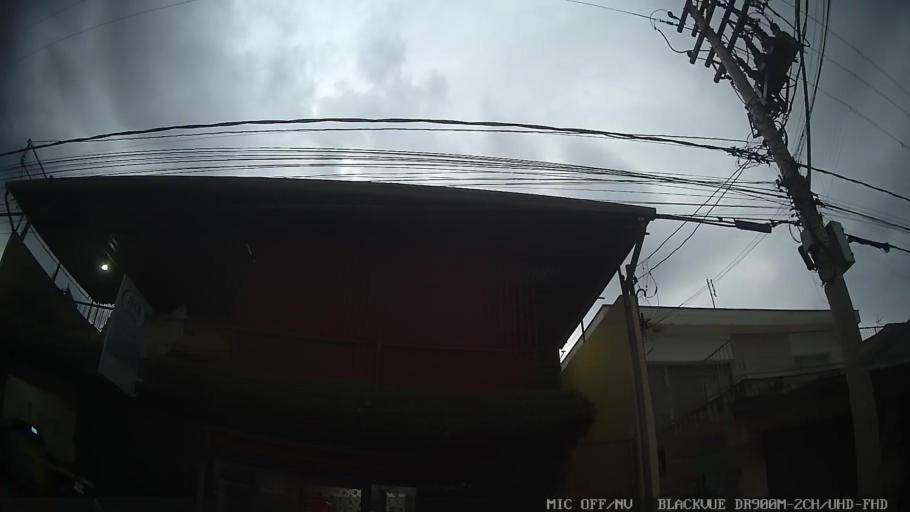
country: BR
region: Sao Paulo
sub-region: Amparo
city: Amparo
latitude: -22.7123
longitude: -46.7762
